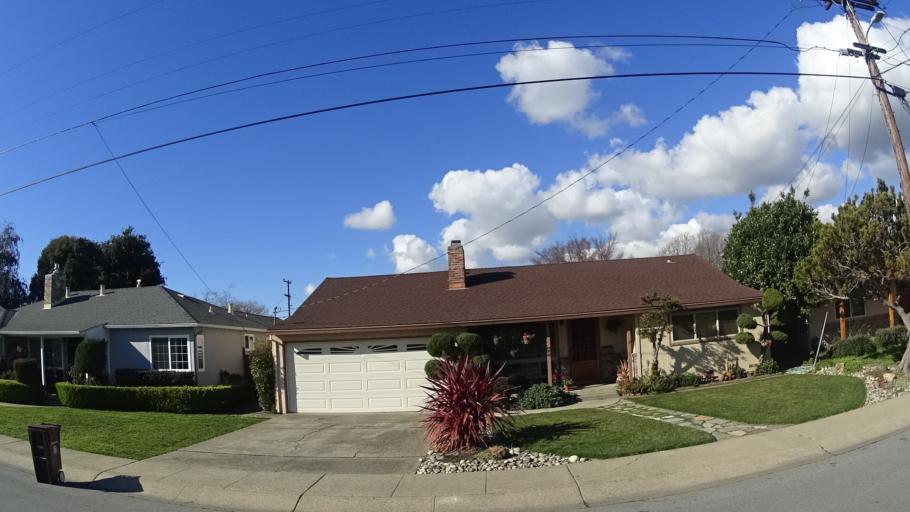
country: US
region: California
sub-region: Alameda County
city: San Lorenzo
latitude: 37.6787
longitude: -122.1162
